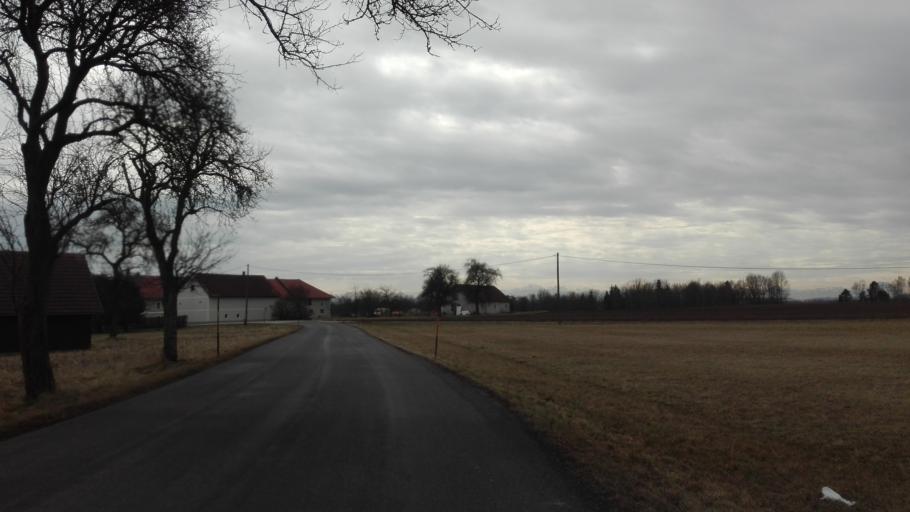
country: AT
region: Upper Austria
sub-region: Politischer Bezirk Linz-Land
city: Traun
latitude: 48.2406
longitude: 14.2188
